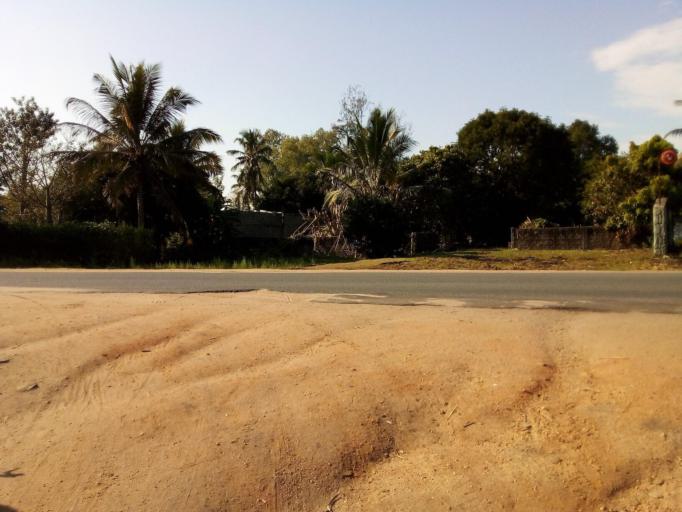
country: MZ
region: Zambezia
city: Quelimane
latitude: -17.5987
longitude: 36.8081
